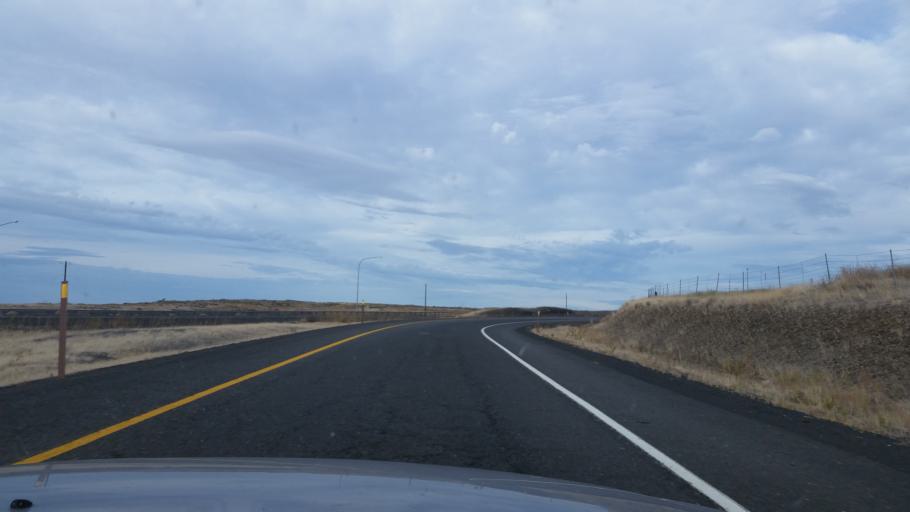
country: US
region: Washington
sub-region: Lincoln County
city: Davenport
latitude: 47.3088
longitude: -117.9698
